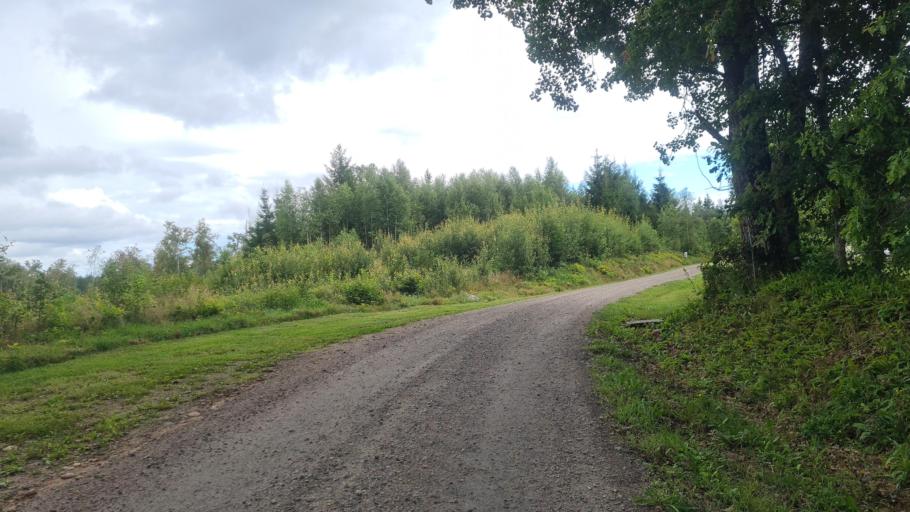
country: SE
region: Kronoberg
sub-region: Ljungby Kommun
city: Ljungby
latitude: 56.8221
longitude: 13.8628
